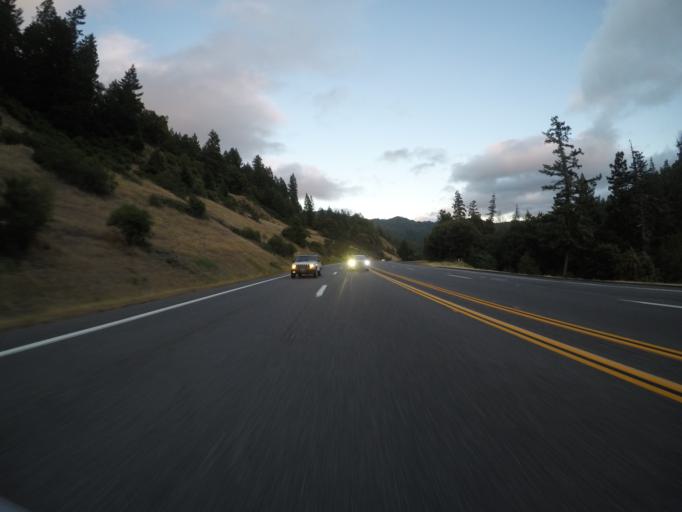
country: US
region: California
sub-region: Humboldt County
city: Redway
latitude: 40.0469
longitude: -123.7846
